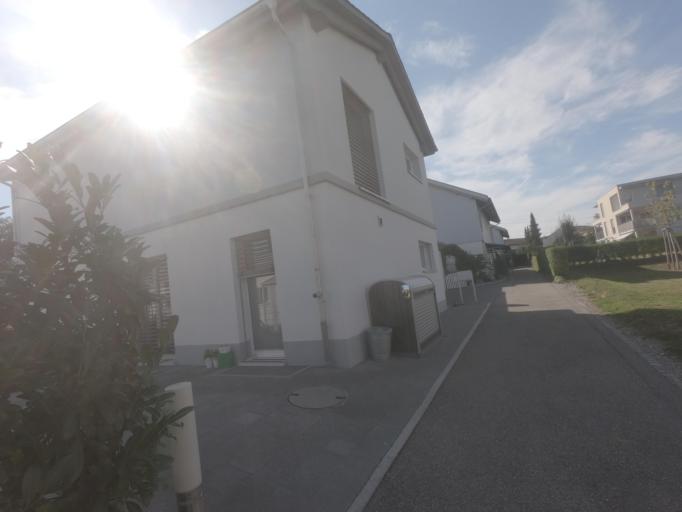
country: CH
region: Bern
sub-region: Bern-Mittelland District
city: Jegenstorf
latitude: 47.0550
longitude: 7.5118
